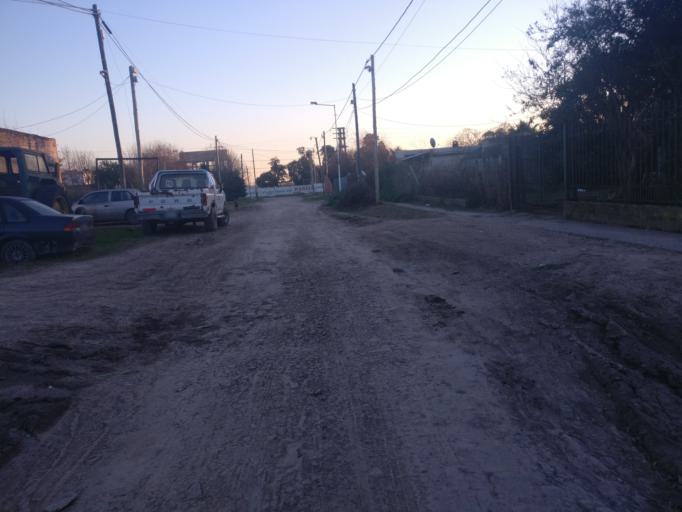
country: AR
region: Buenos Aires
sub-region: Partido de Ezeiza
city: Ezeiza
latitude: -34.9442
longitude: -58.6126
